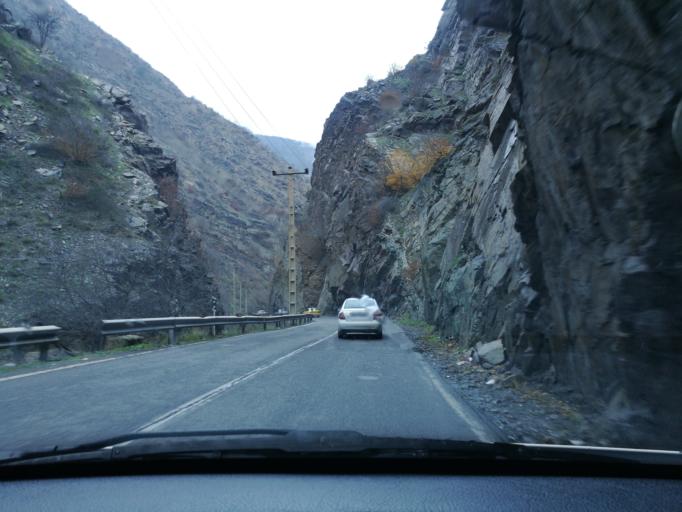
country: IR
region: Mazandaran
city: Chalus
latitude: 36.2813
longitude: 51.2432
